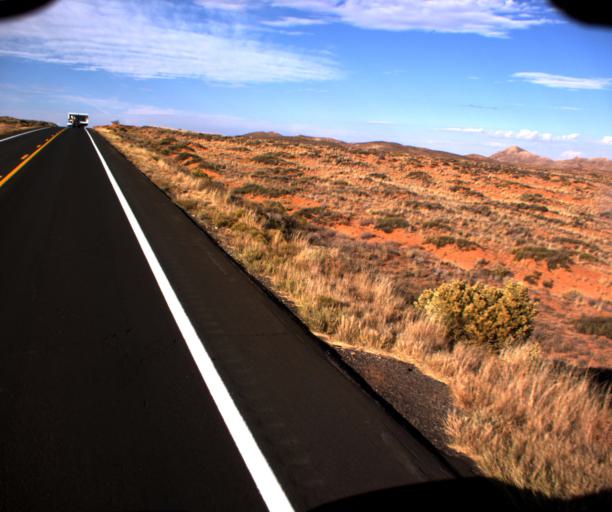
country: US
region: Arizona
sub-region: Apache County
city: Lukachukai
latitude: 36.9532
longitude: -109.5106
